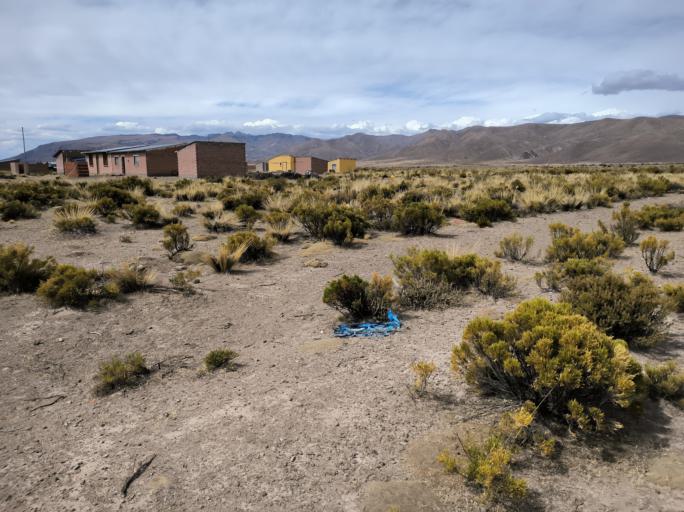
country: BO
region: Oruro
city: Challapata
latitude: -19.1208
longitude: -66.7685
